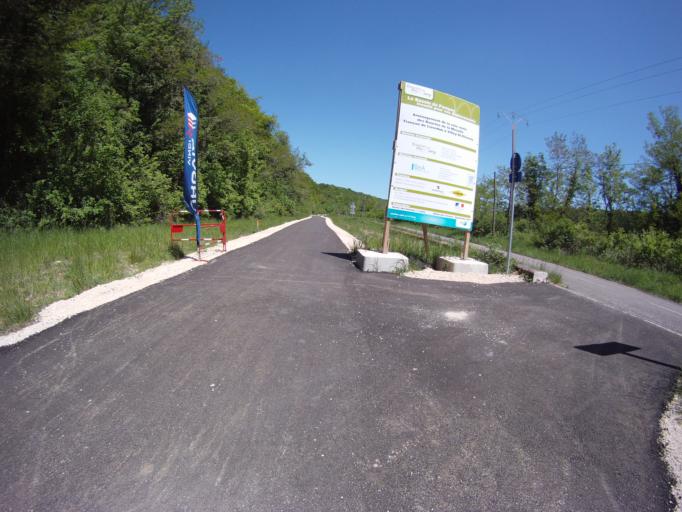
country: FR
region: Lorraine
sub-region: Departement de Meurthe-et-Moselle
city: Villey-Saint-Etienne
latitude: 48.7477
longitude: 6.0066
